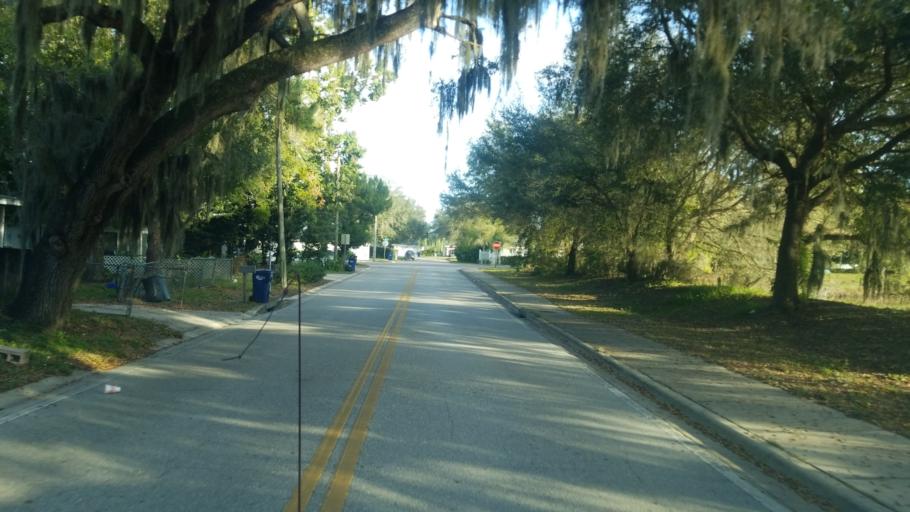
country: US
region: Florida
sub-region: Manatee County
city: Samoset
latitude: 27.4504
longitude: -82.5342
